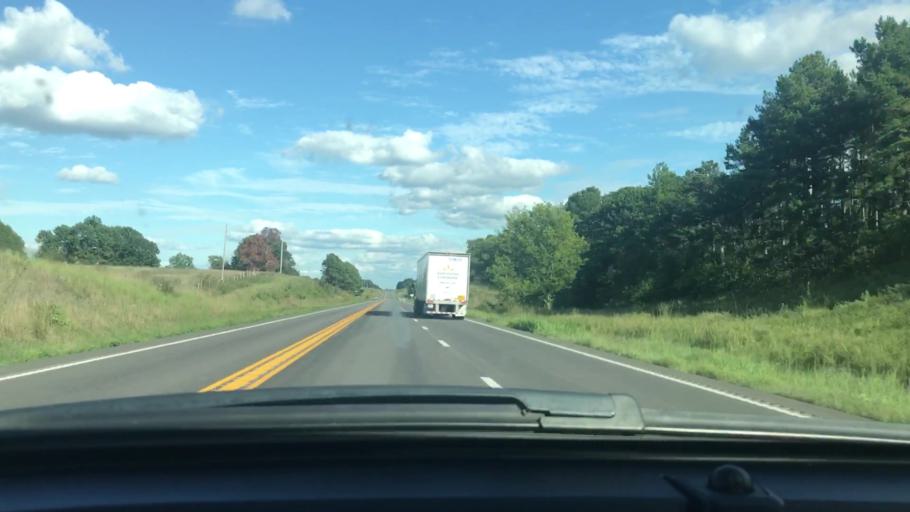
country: US
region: Missouri
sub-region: Oregon County
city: Thayer
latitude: 36.5873
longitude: -91.6313
